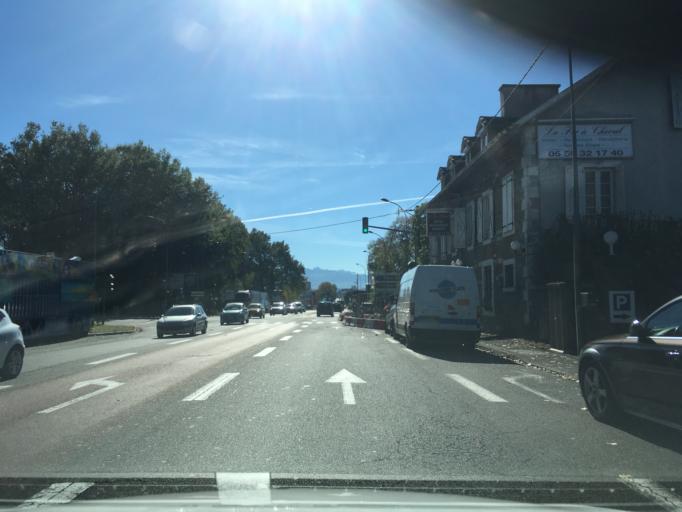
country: FR
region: Aquitaine
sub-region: Departement des Pyrenees-Atlantiques
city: Lons
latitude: 43.3360
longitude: -0.3798
